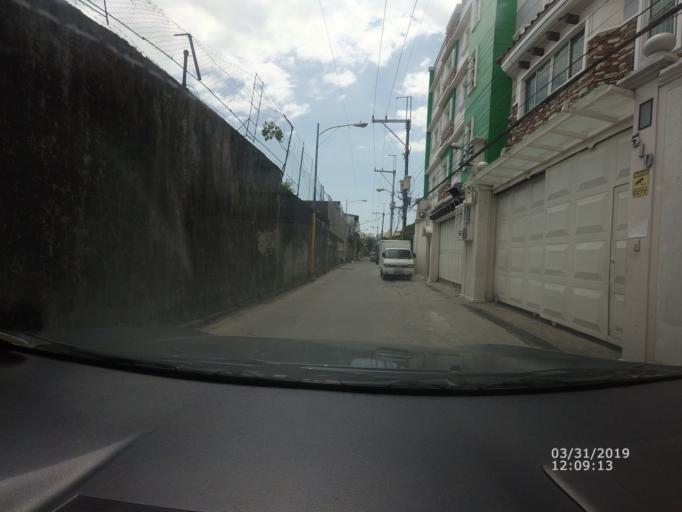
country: PH
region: Metro Manila
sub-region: Mandaluyong
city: Mandaluyong City
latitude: 14.5793
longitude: 121.0292
